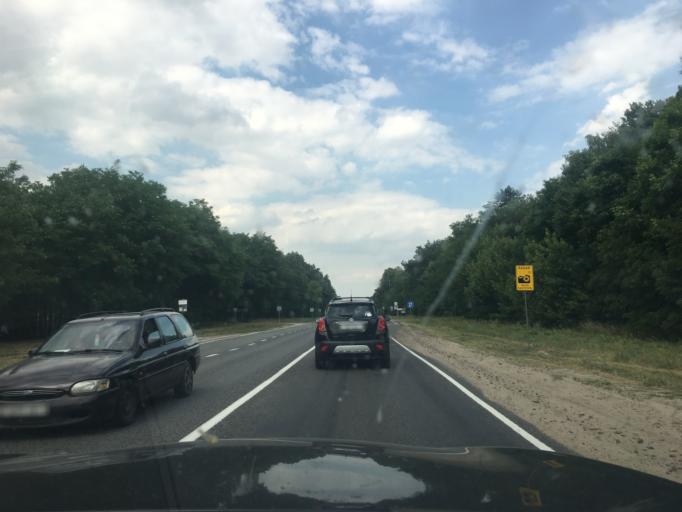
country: BY
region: Brest
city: Charnawchytsy
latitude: 52.1665
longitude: 23.7043
